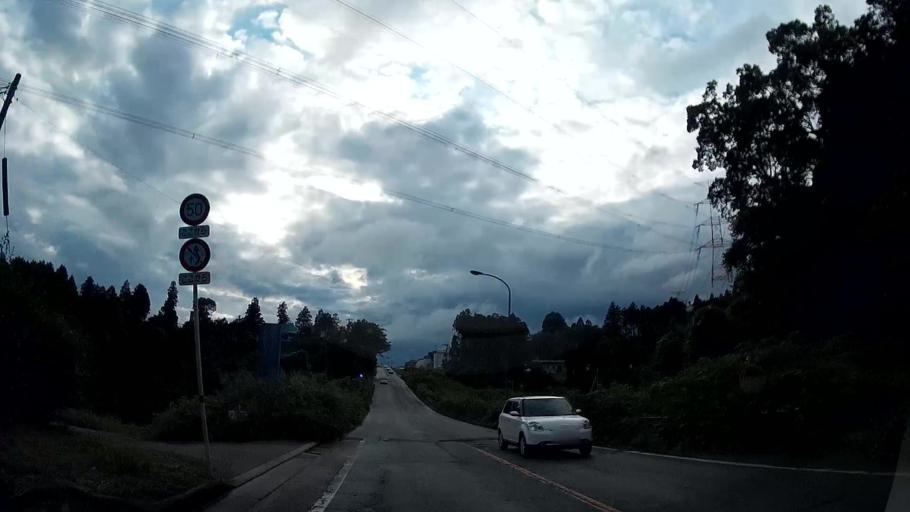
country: JP
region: Kumamoto
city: Ozu
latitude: 32.8766
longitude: 130.9242
